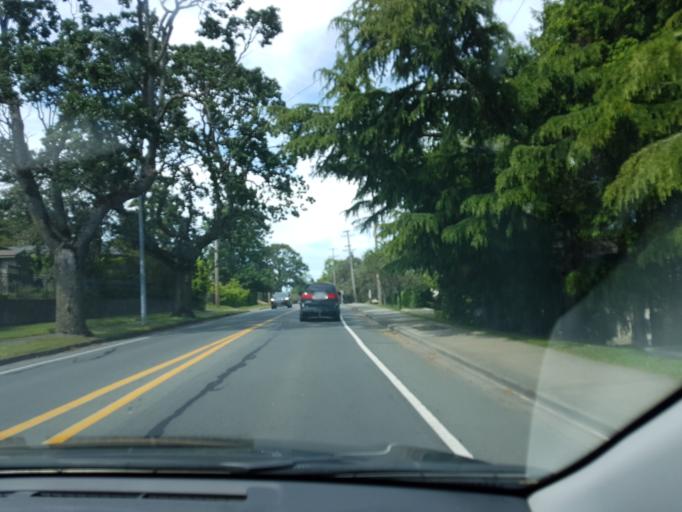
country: CA
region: British Columbia
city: Oak Bay
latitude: 48.4697
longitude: -123.3351
